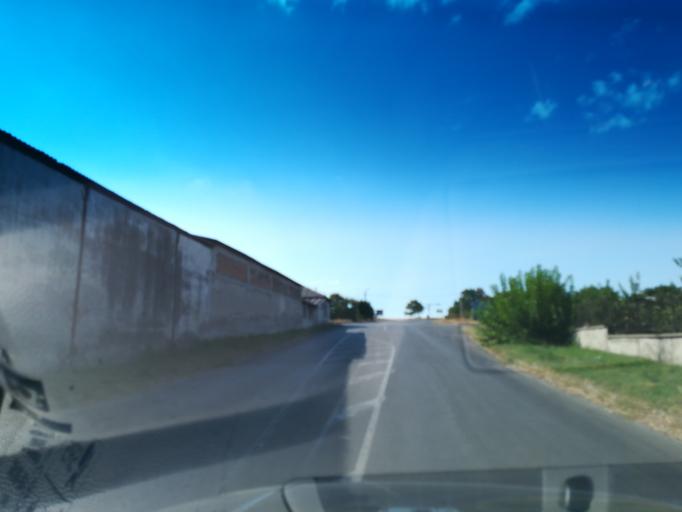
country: BG
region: Khaskovo
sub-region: Obshtina Mineralni Bani
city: Mineralni Bani
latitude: 42.0206
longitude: 25.4139
